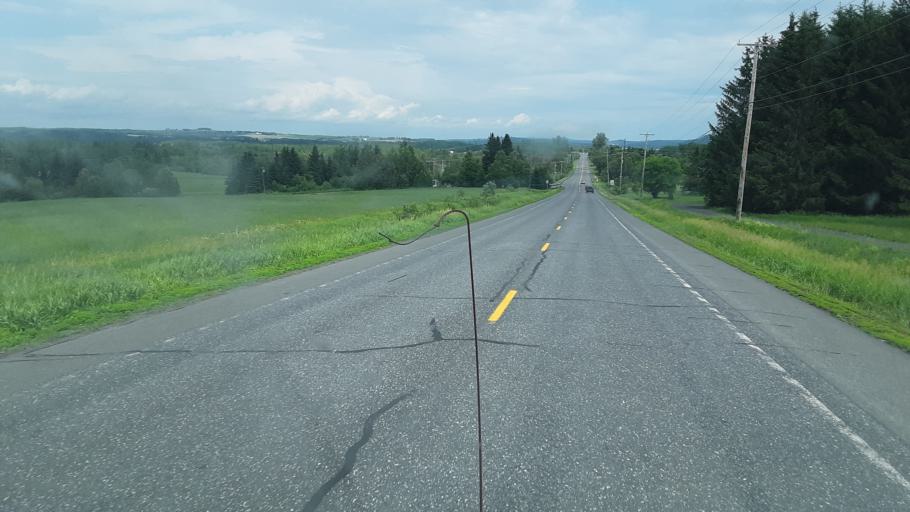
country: US
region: Maine
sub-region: Aroostook County
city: Fort Fairfield
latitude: 46.7585
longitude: -67.8615
